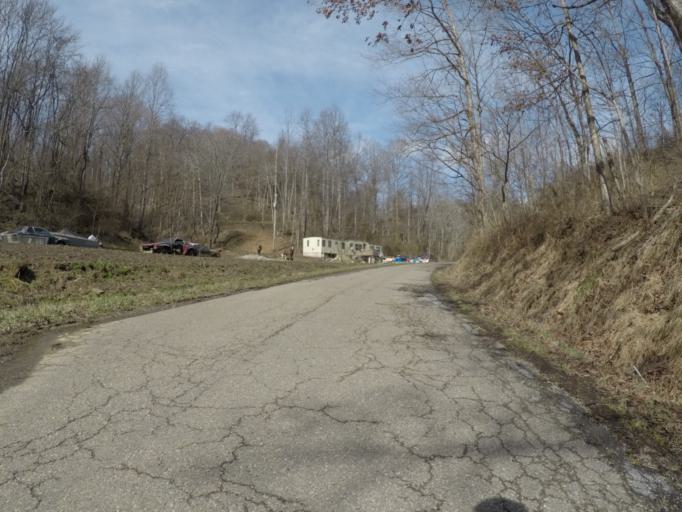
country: US
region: Ohio
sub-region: Lawrence County
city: Burlington
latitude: 38.4822
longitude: -82.5336
